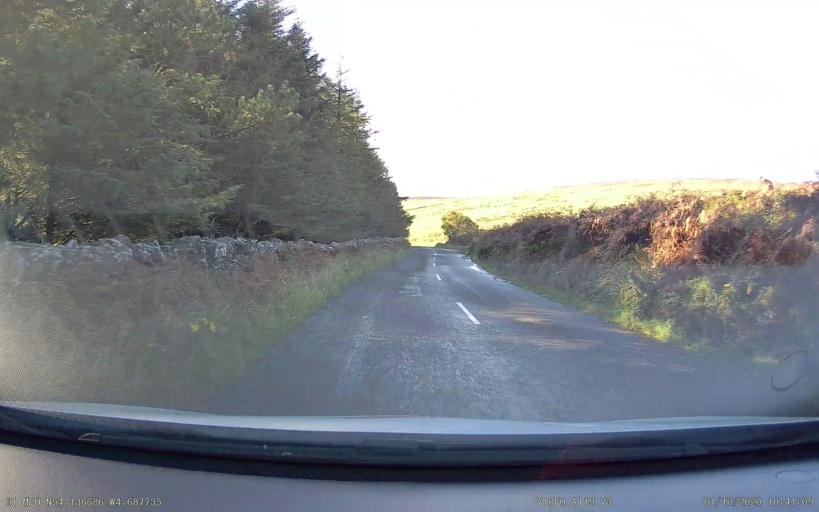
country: IM
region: Castletown
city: Castletown
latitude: 54.1367
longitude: -4.6877
